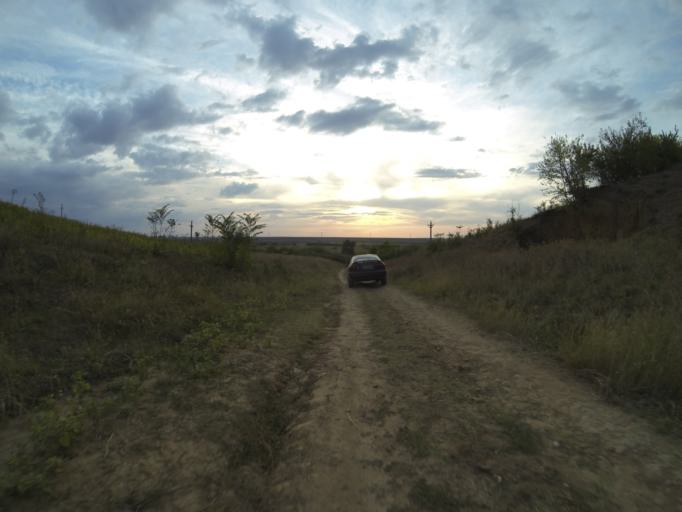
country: RO
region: Dolj
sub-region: Comuna Ceratu
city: Ceratu
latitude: 44.0870
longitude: 23.6740
